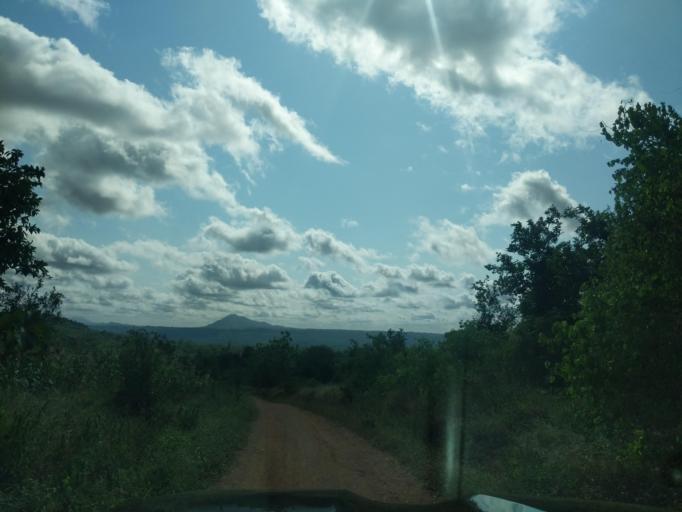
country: TZ
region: Tanga
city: Muheza
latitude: -5.4209
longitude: 38.6417
